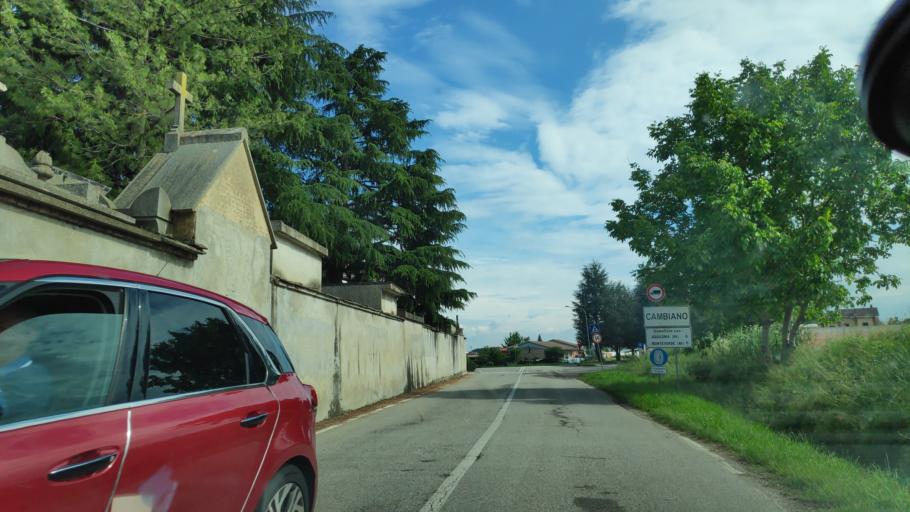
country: IT
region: Piedmont
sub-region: Provincia di Torino
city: Cambiano
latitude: 44.9801
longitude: 7.7821
